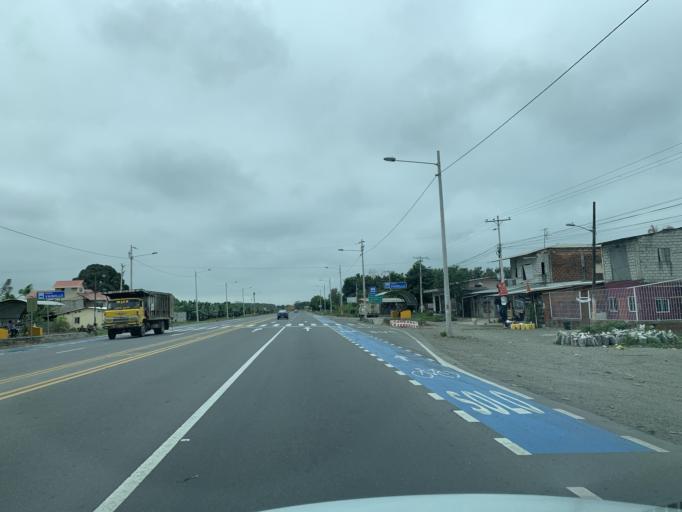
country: EC
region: Guayas
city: Coronel Marcelino Mariduena
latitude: -2.3163
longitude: -79.4696
